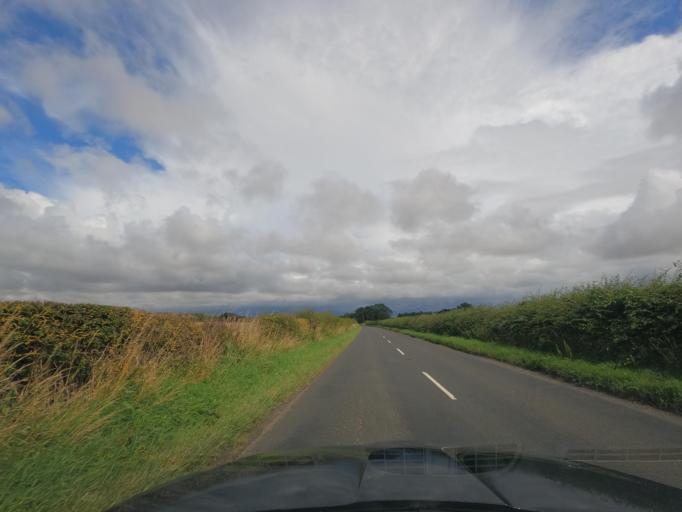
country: GB
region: England
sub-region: Northumberland
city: Lowick
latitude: 55.6592
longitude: -1.9960
